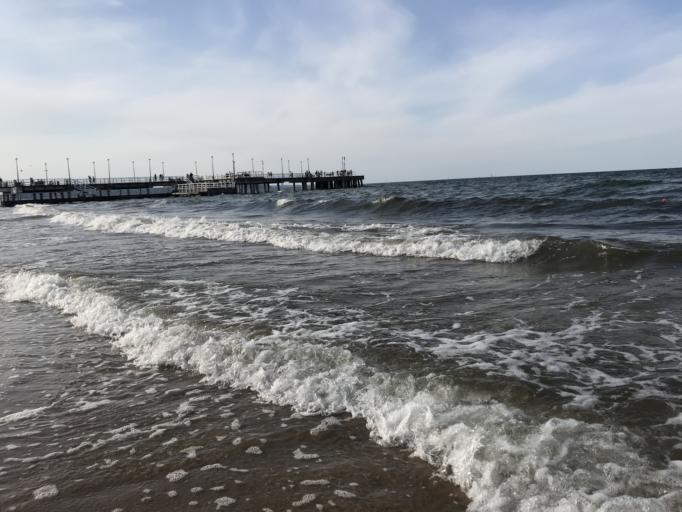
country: PL
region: Pomeranian Voivodeship
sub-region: Gdansk
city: Gdansk
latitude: 54.4134
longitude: 18.6262
